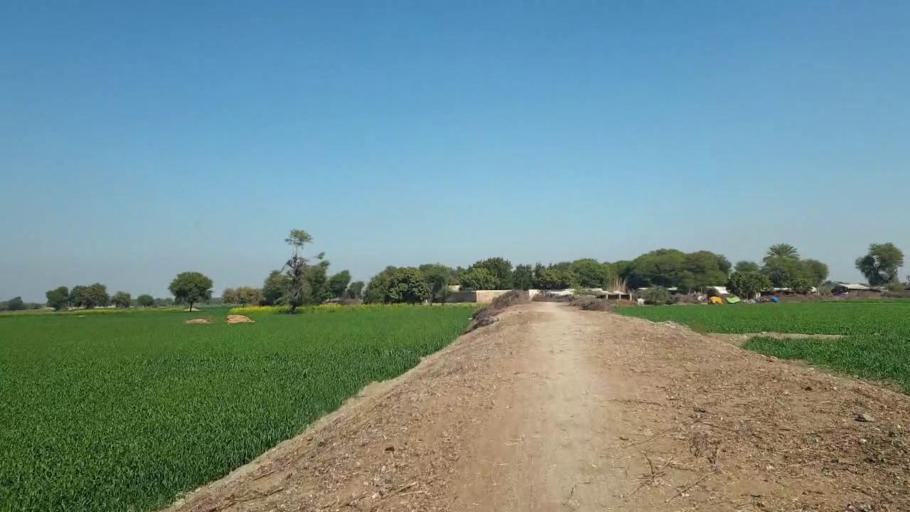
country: PK
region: Sindh
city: Shahpur Chakar
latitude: 26.1230
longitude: 68.6452
